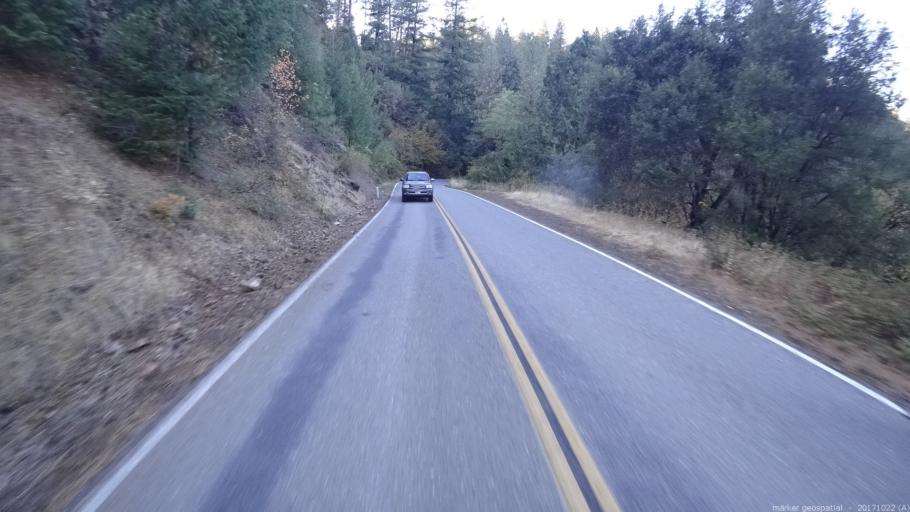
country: US
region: California
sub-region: Shasta County
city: Shasta Lake
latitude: 40.9059
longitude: -122.2367
